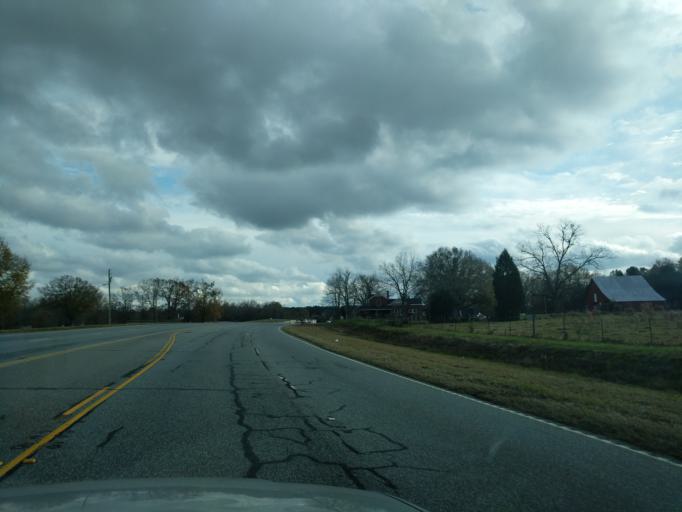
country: US
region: South Carolina
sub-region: Greenwood County
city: Ware Shoals
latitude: 34.4643
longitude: -82.2552
